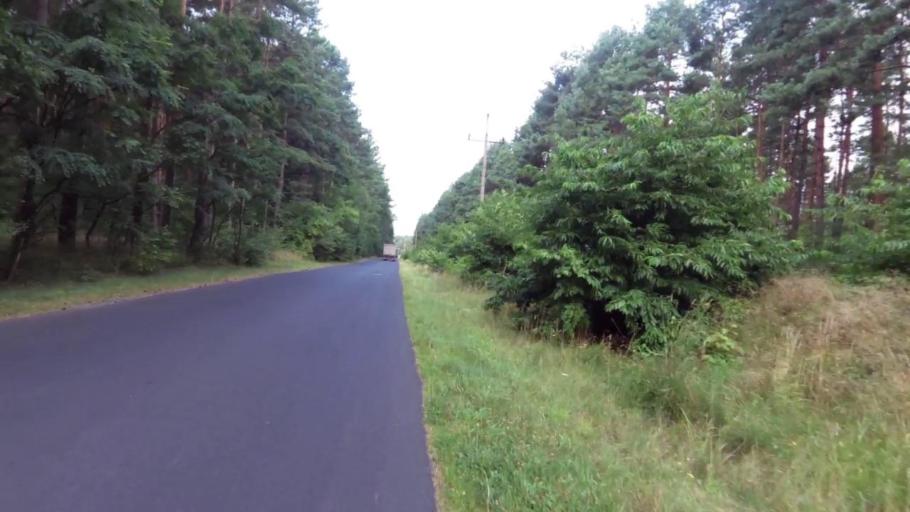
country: PL
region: West Pomeranian Voivodeship
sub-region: Powiat mysliborski
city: Debno
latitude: 52.8492
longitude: 14.7370
